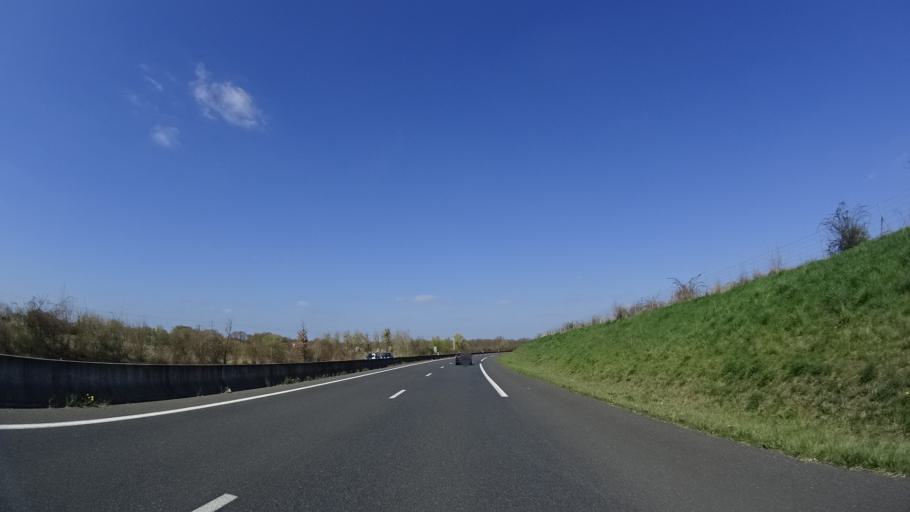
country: FR
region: Pays de la Loire
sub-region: Departement de Maine-et-Loire
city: Saint-Jean
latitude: 47.2933
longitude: -0.3875
